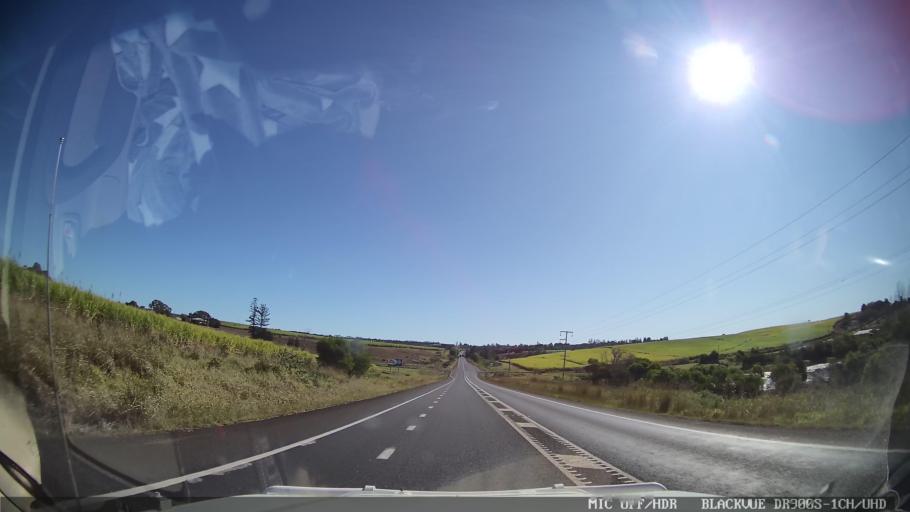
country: AU
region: Queensland
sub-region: Bundaberg
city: Childers
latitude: -25.2453
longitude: 152.3117
